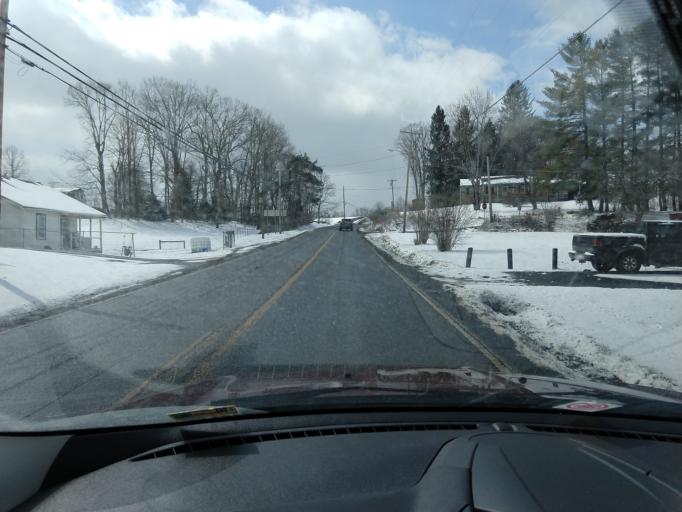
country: US
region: West Virginia
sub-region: Nicholas County
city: Craigsville
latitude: 38.3314
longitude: -80.6452
